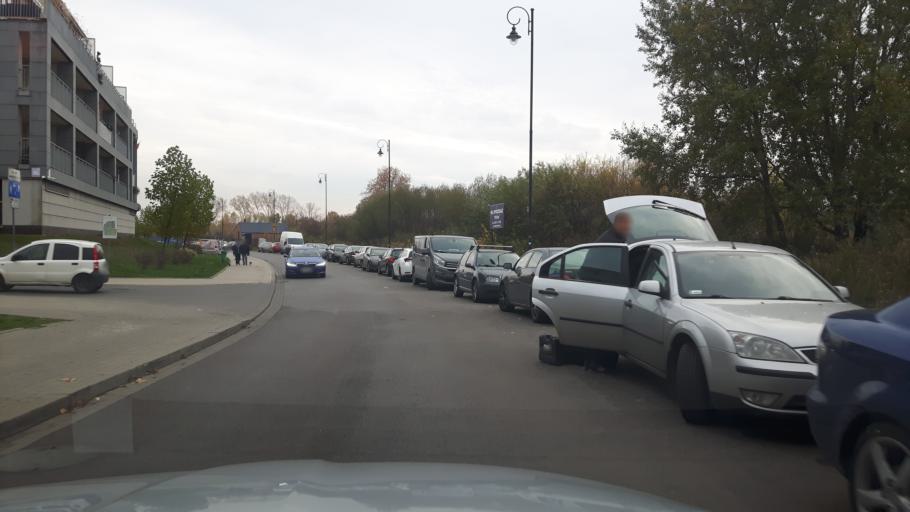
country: PL
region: Masovian Voivodeship
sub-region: Warszawa
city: Ursynow
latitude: 52.1614
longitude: 21.0639
